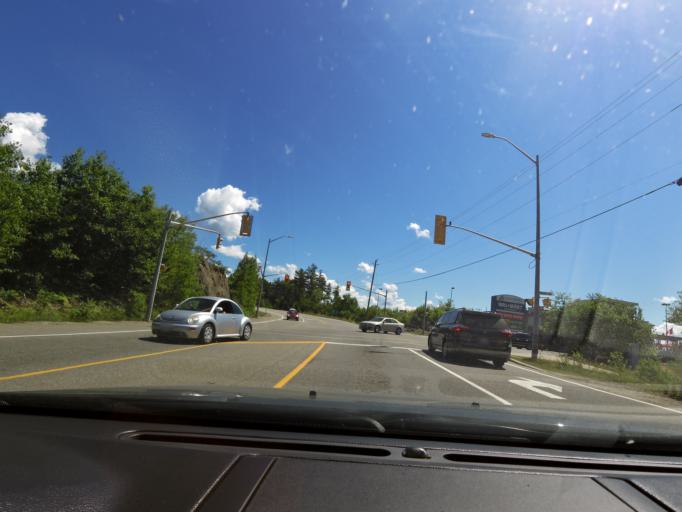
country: CA
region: Ontario
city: Bracebridge
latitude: 45.0504
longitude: -79.2933
